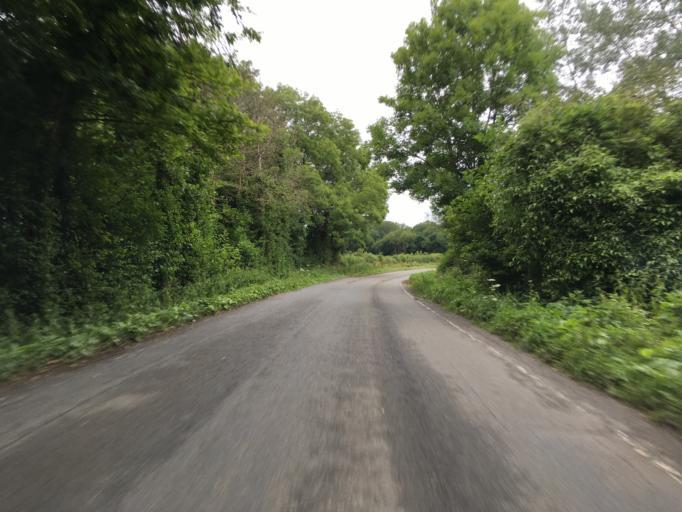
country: GB
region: England
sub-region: Gloucestershire
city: Dursley
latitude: 51.7822
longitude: -2.3918
